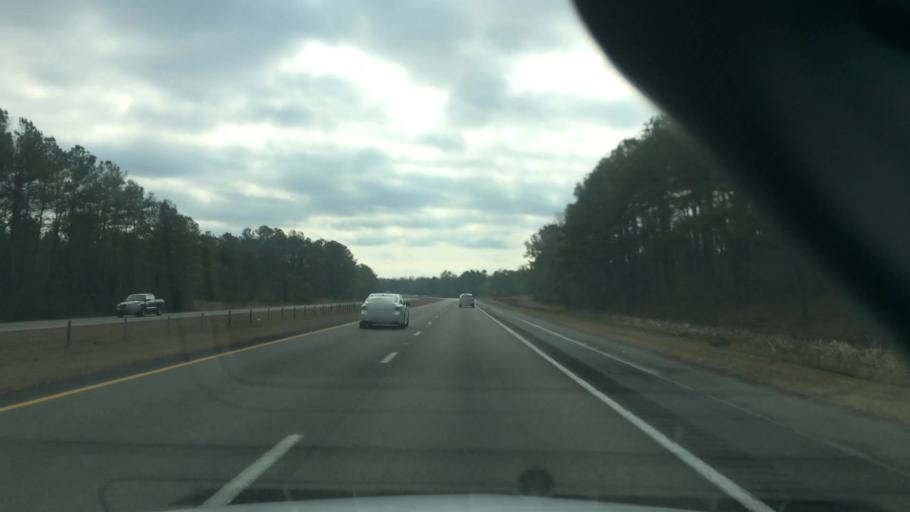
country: US
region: North Carolina
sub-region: New Hanover County
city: Castle Hayne
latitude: 34.3763
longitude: -77.8841
